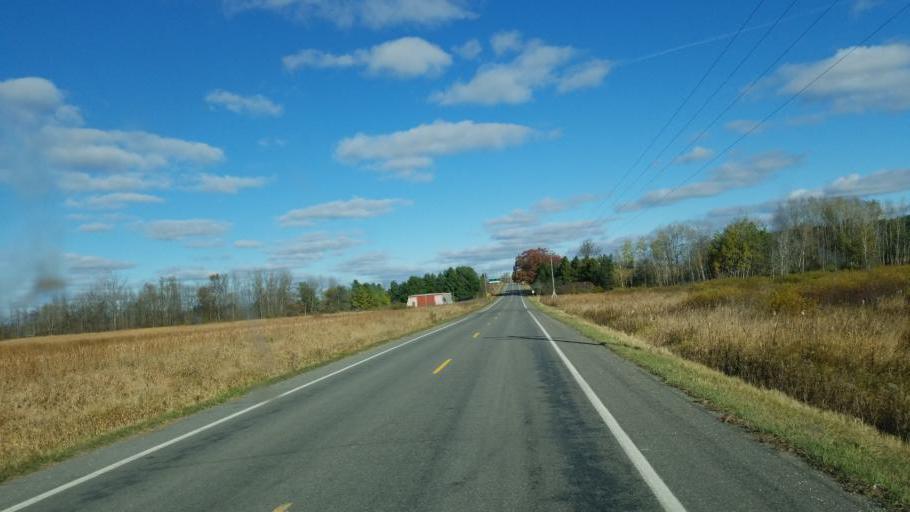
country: US
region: Michigan
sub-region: Montcalm County
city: Edmore
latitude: 43.4451
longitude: -85.0442
